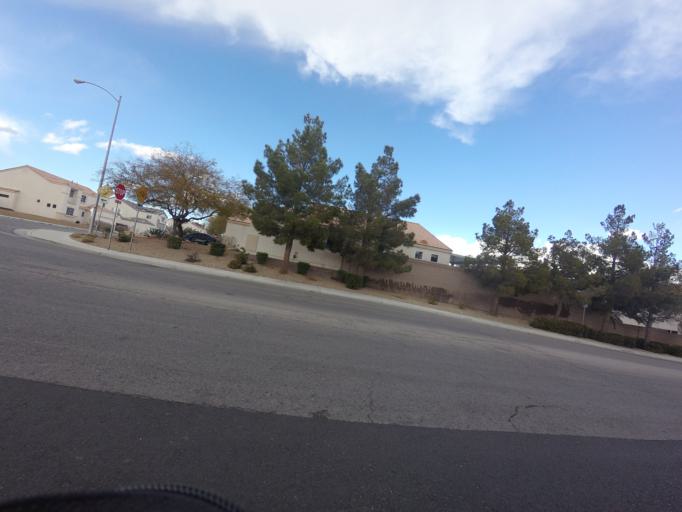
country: US
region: Nevada
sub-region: Clark County
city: North Las Vegas
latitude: 36.2652
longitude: -115.1932
